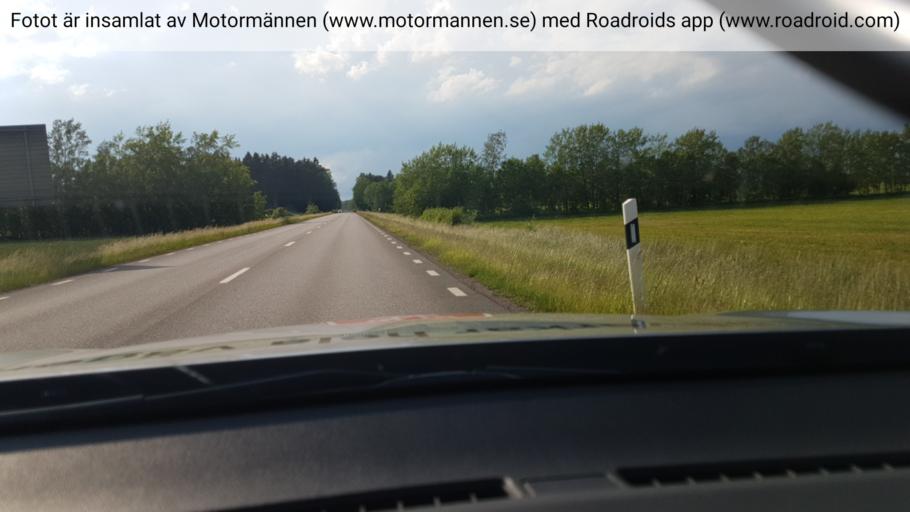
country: SE
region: Vaestra Goetaland
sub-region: Tidaholms Kommun
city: Olofstorp
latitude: 58.3561
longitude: 14.0450
